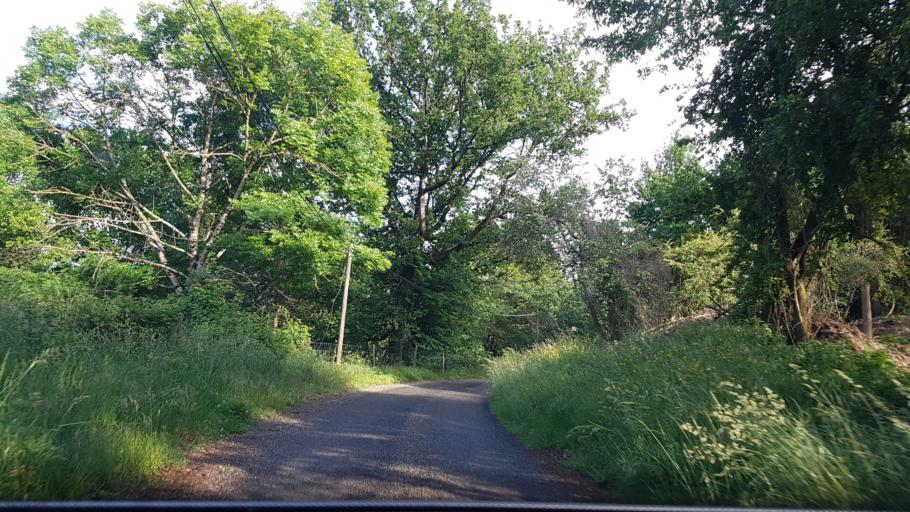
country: FR
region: Midi-Pyrenees
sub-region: Departement de l'Ariege
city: La Tour-du-Crieu
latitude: 43.1169
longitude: 1.7184
